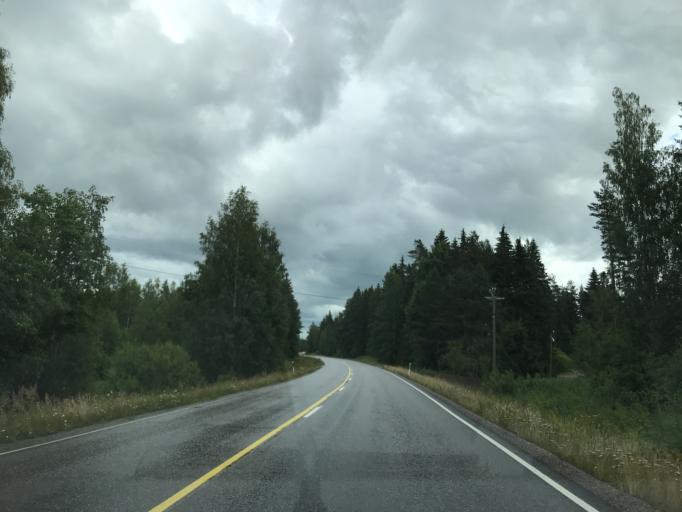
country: FI
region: Uusimaa
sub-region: Porvoo
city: Pukkila
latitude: 60.7683
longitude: 25.5111
